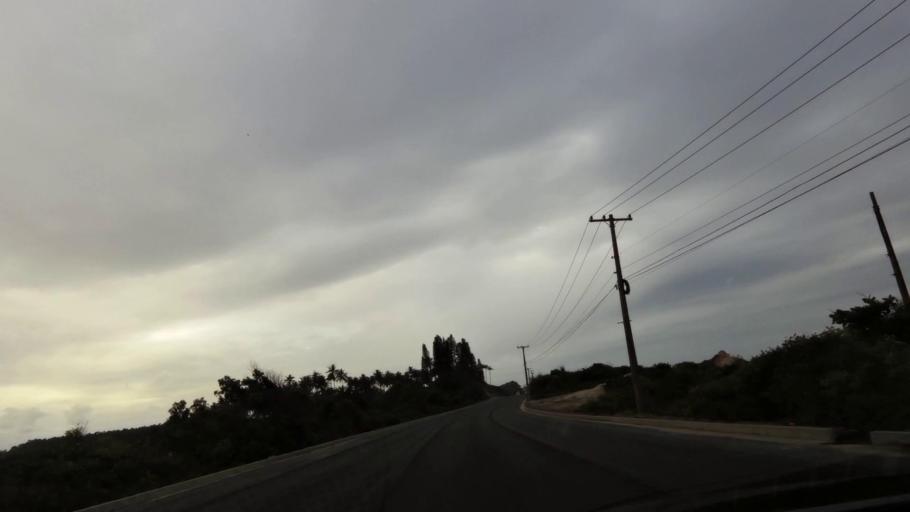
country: BR
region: Espirito Santo
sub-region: Guarapari
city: Guarapari
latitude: -20.7648
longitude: -40.5711
